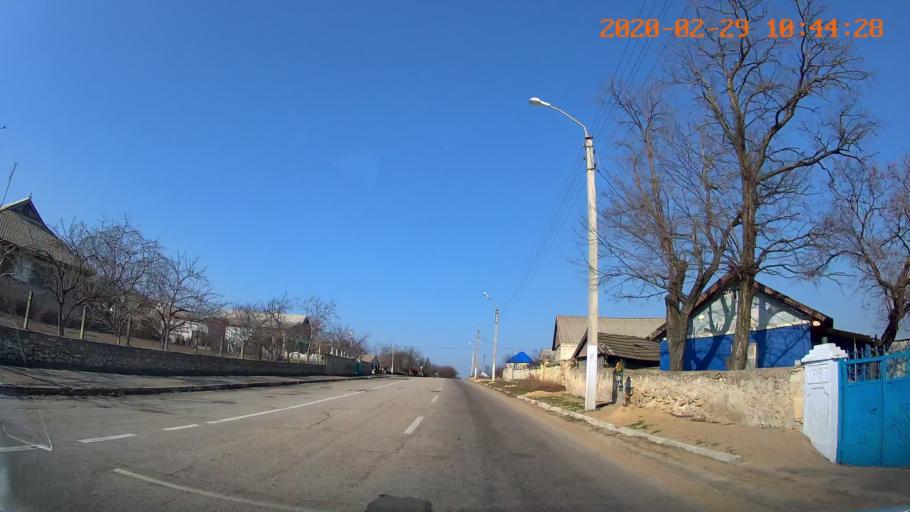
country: MD
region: Telenesti
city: Grigoriopol
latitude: 47.0704
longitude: 29.3945
